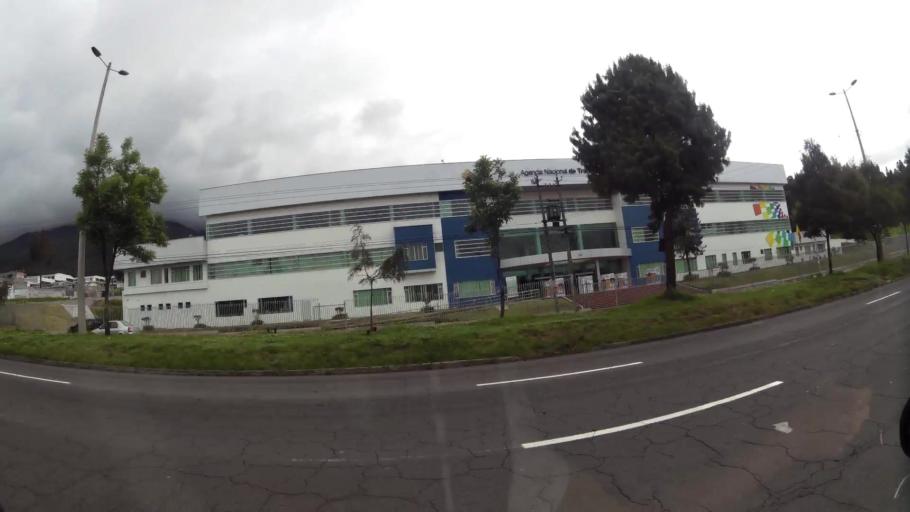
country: EC
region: Pichincha
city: Quito
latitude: -0.1378
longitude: -78.5013
